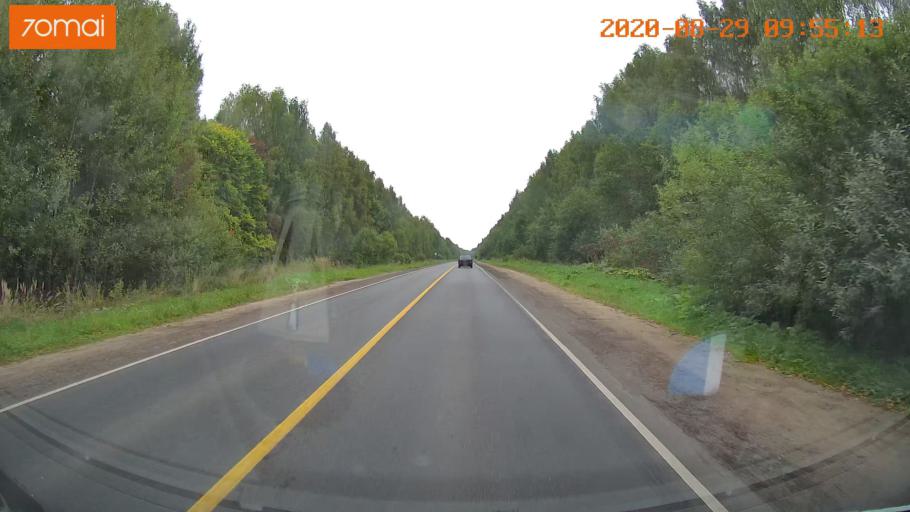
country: RU
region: Ivanovo
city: Zarechnyy
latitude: 57.4226
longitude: 42.2575
